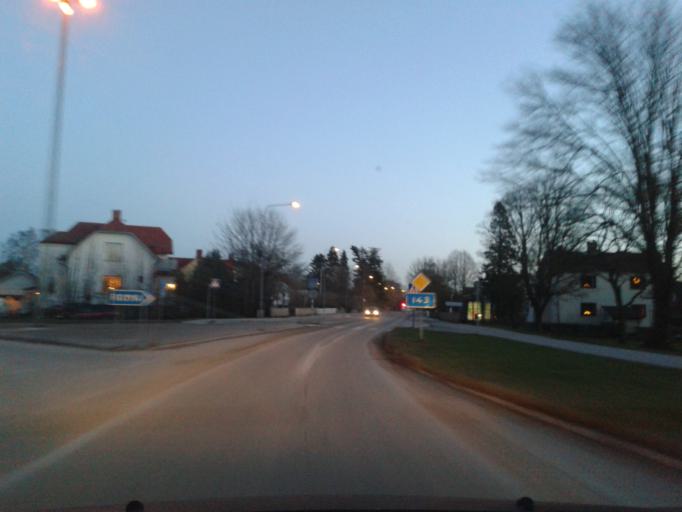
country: SE
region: Gotland
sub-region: Gotland
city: Visby
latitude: 57.6347
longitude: 18.3077
